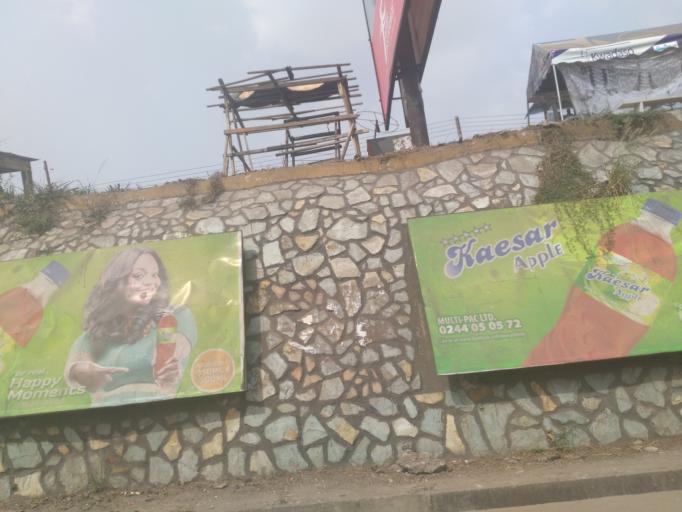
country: GH
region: Ashanti
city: Kumasi
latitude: 6.6871
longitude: -1.5757
